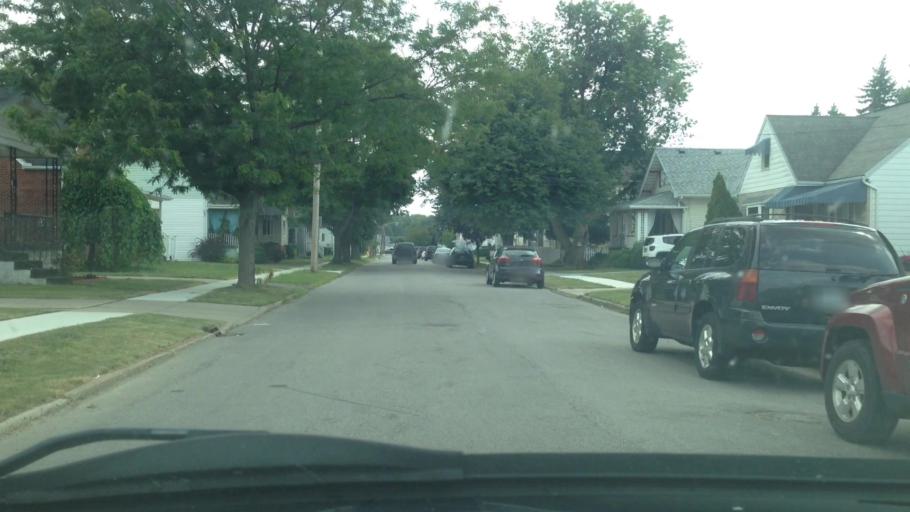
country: US
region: New York
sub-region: Erie County
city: Sloan
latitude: 42.8743
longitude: -78.7969
